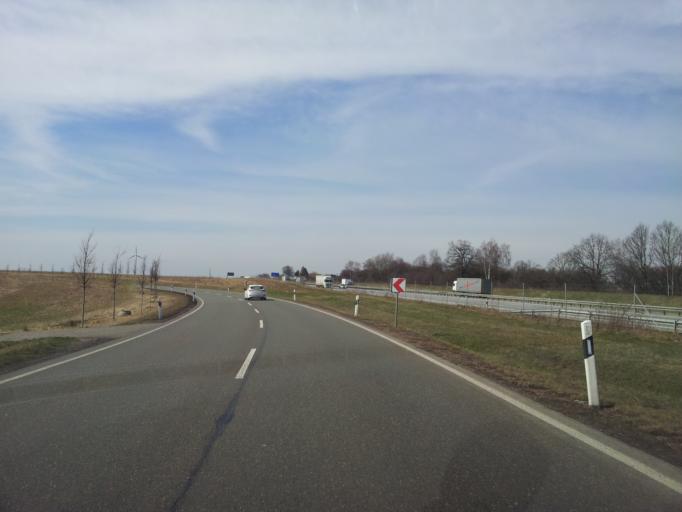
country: DE
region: Saxony
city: Callenberg
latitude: 50.8167
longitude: 12.6567
